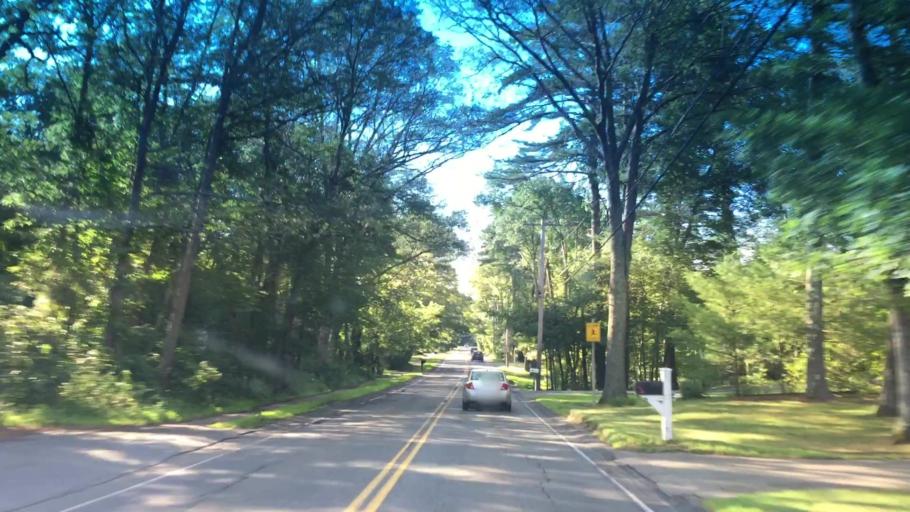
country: US
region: Massachusetts
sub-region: Norfolk County
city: Norfolk
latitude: 42.1307
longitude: -71.3352
